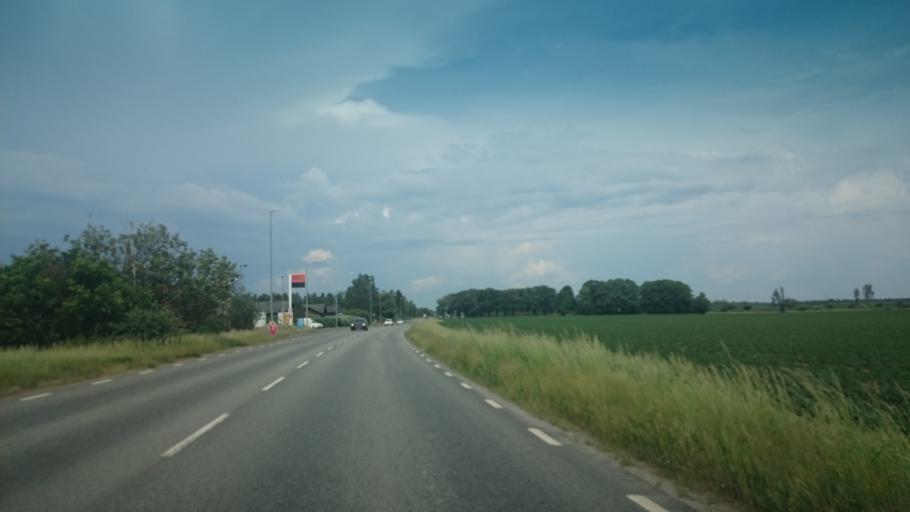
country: SE
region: Skane
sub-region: Kristianstads Kommun
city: Norra Asum
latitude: 55.9977
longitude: 14.1511
